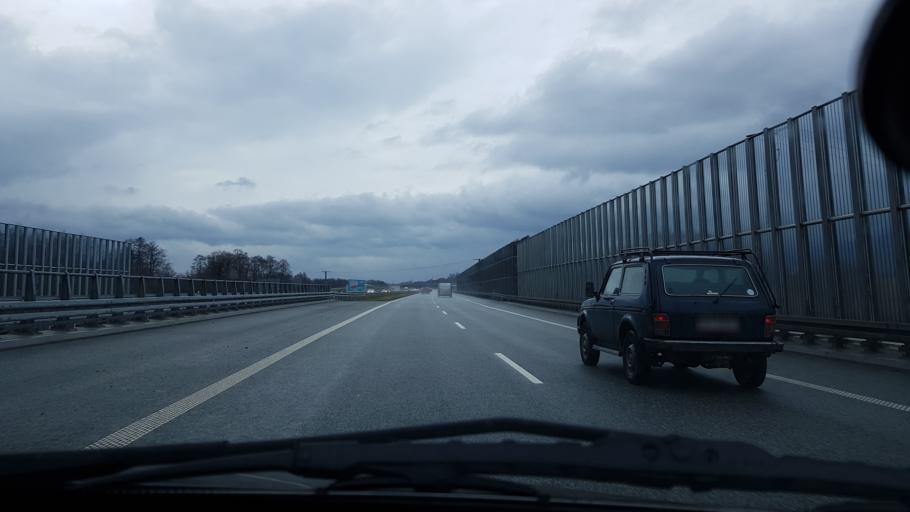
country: PL
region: Silesian Voivodeship
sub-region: Powiat bielski
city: Wilkowice
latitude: 49.7564
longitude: 19.0869
